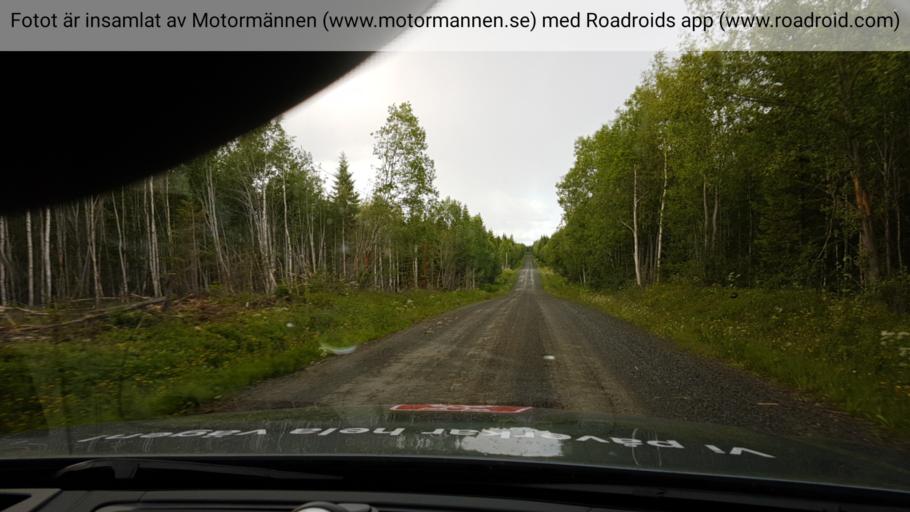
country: SE
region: Jaemtland
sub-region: Bergs Kommun
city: Hoverberg
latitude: 62.9647
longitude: 14.2329
